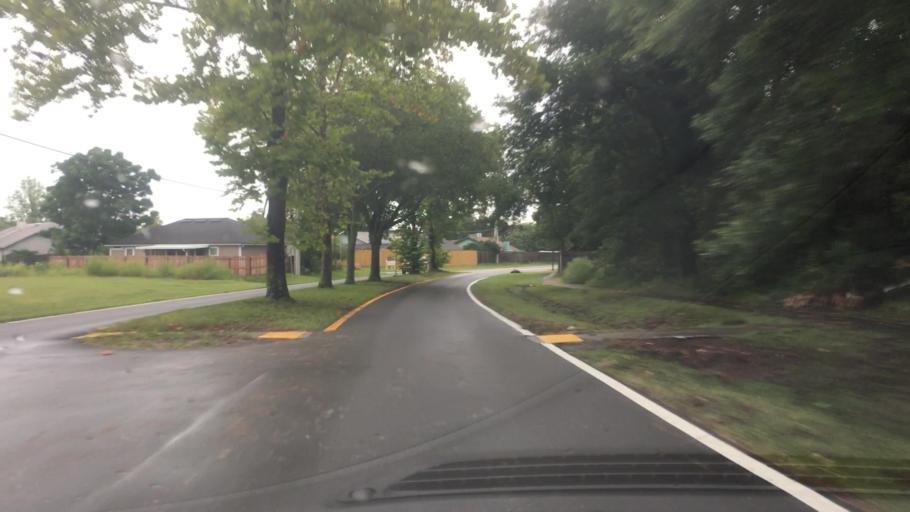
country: US
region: Florida
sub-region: Duval County
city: Atlantic Beach
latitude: 30.3258
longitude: -81.4630
